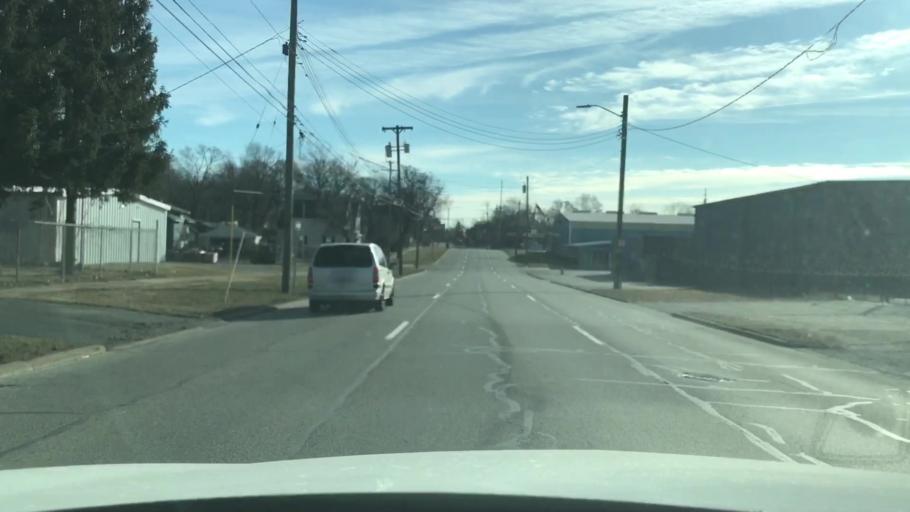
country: US
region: Michigan
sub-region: Oakland County
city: Pontiac
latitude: 42.6464
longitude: -83.3065
